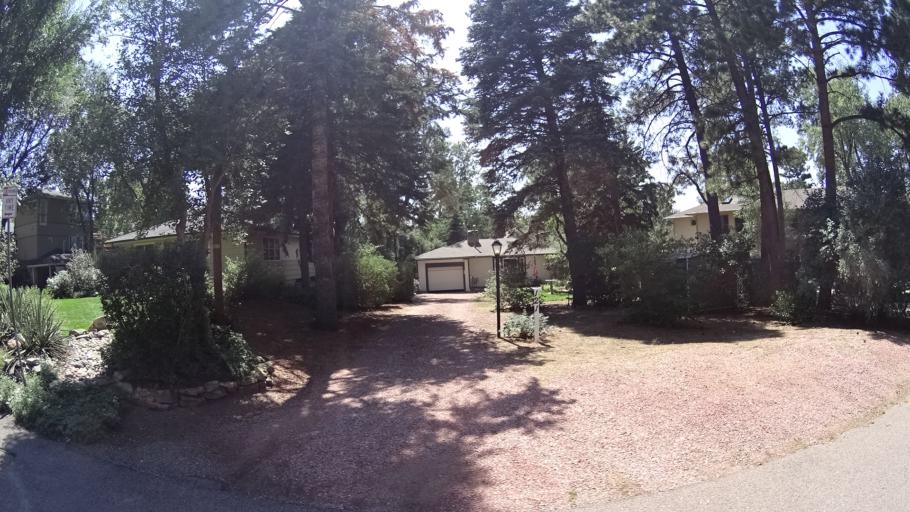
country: US
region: Colorado
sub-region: El Paso County
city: Colorado Springs
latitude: 38.8658
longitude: -104.8265
